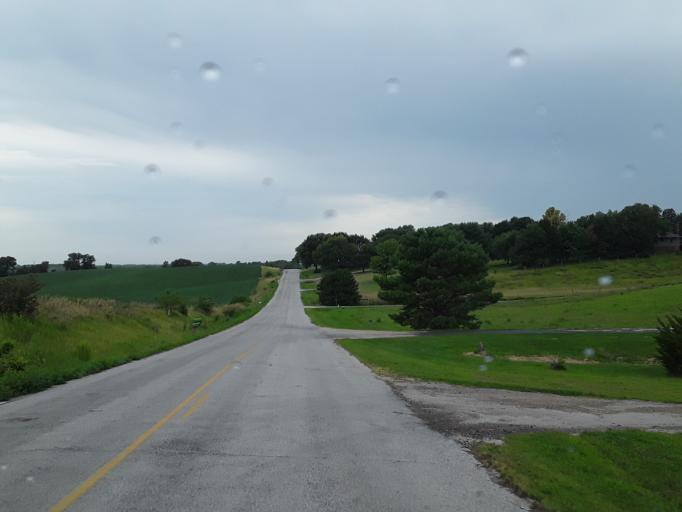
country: US
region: Nebraska
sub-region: Washington County
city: Blair
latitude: 41.5018
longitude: -96.1493
